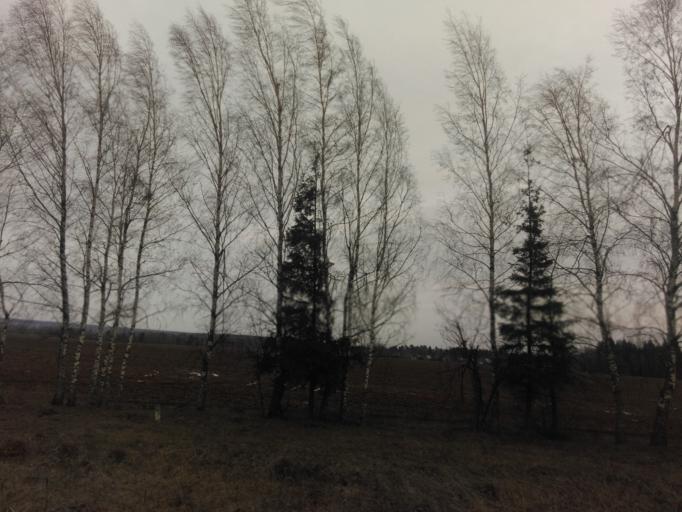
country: RU
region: Moskovskaya
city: Kolyubakino
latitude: 55.6352
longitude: 36.5390
